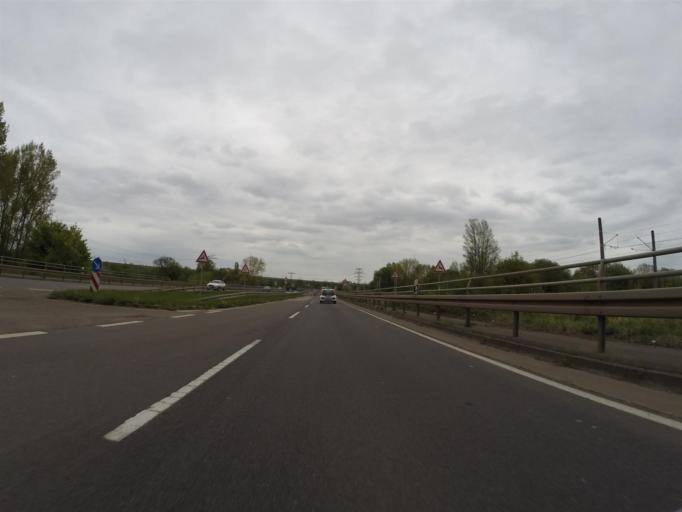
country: DE
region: Saxony-Anhalt
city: Schkopau
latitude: 51.4070
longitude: 11.9791
